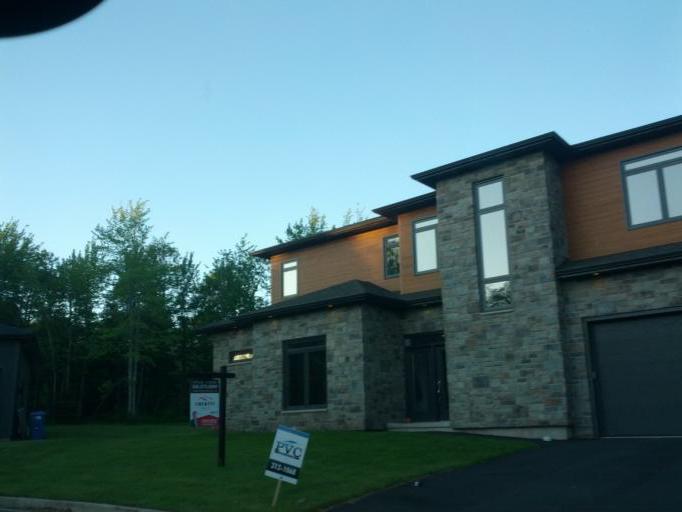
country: CA
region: New Brunswick
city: Moncton
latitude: 46.1122
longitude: -64.8714
